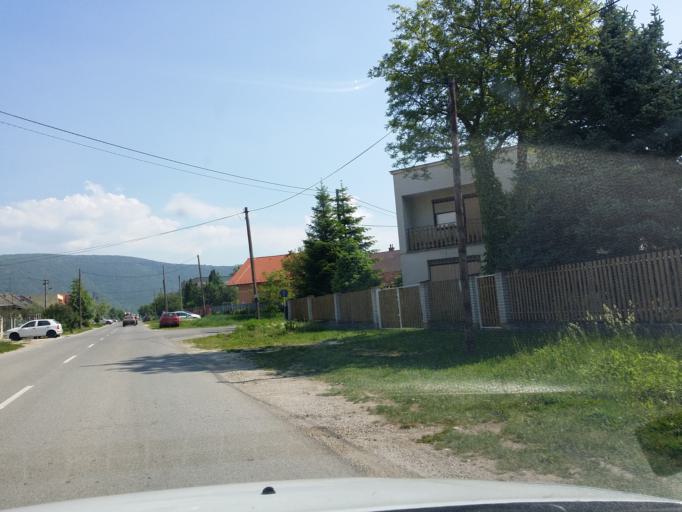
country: SK
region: Kosicky
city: Medzev
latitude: 48.6024
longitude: 20.8797
